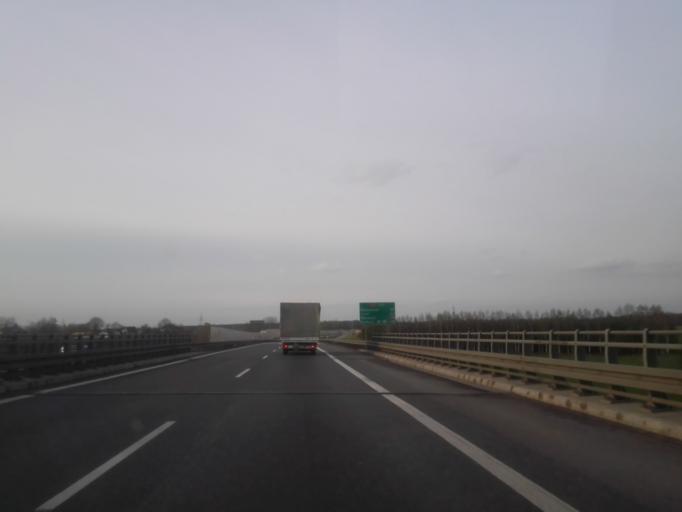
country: PL
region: Lodz Voivodeship
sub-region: Powiat rawski
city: Rawa Mazowiecka
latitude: 51.7773
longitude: 20.2758
